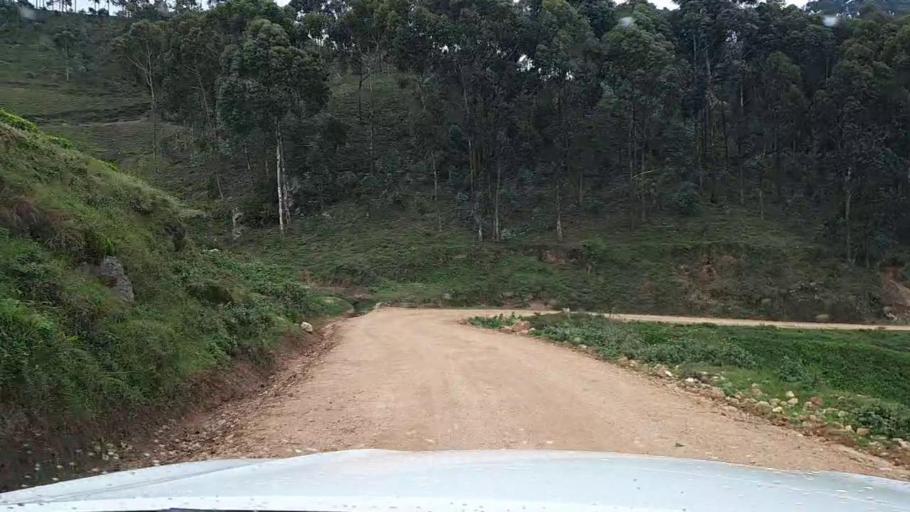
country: RW
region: Western Province
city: Kibuye
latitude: -2.2927
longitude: 29.3819
